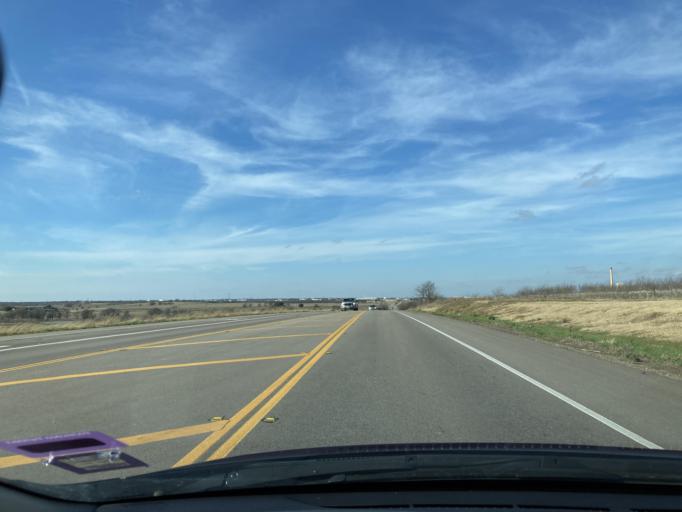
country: US
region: Texas
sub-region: Navarro County
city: Corsicana
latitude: 32.0499
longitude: -96.4203
